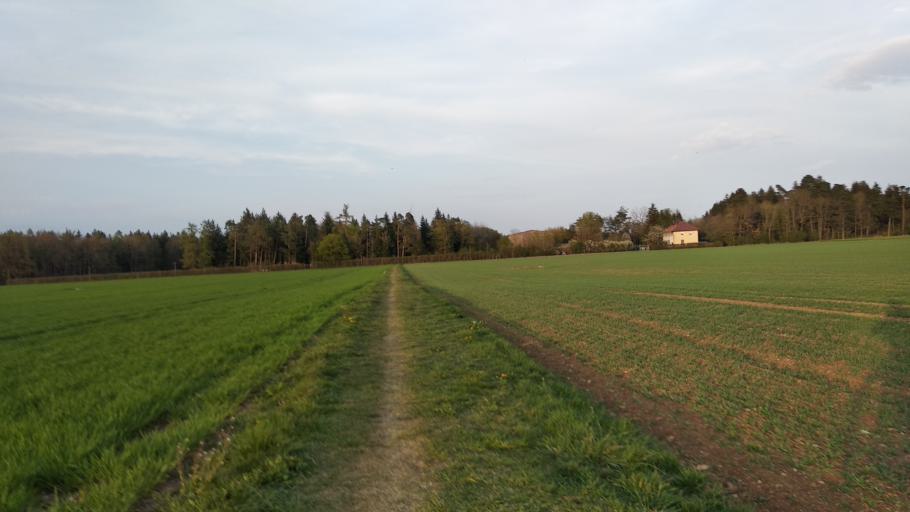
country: DE
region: Bavaria
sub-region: Upper Bavaria
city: Haar
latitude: 48.0976
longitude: 11.7344
